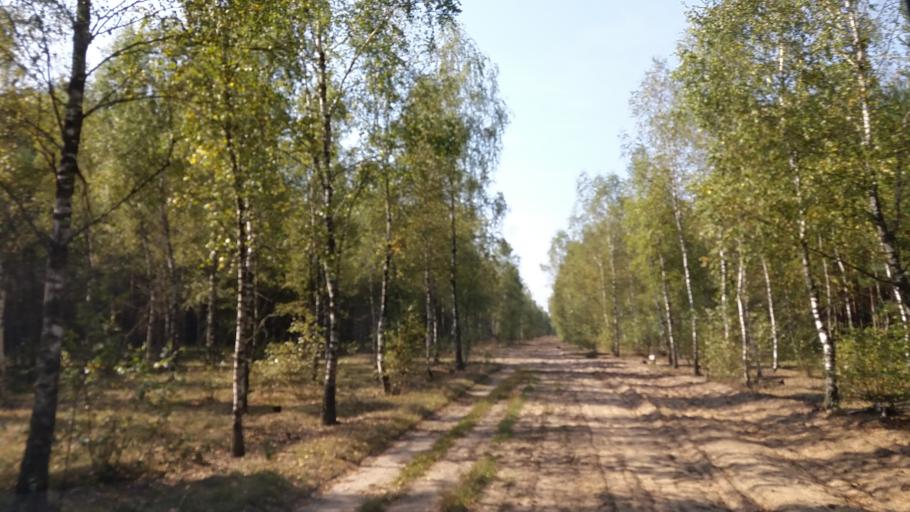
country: PL
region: West Pomeranian Voivodeship
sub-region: Powiat drawski
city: Kalisz Pomorski
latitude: 53.1994
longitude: 15.9849
